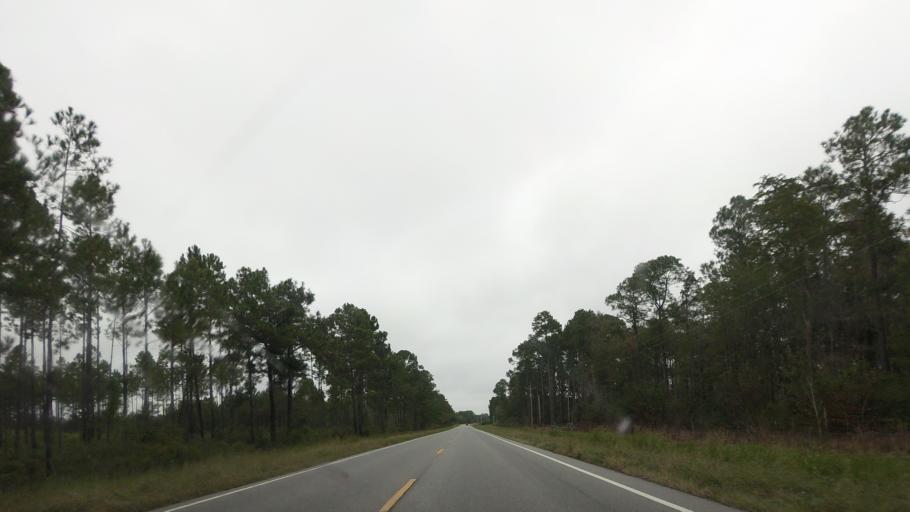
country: US
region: Georgia
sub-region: Berrien County
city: Nashville
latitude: 31.2785
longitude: -83.2395
